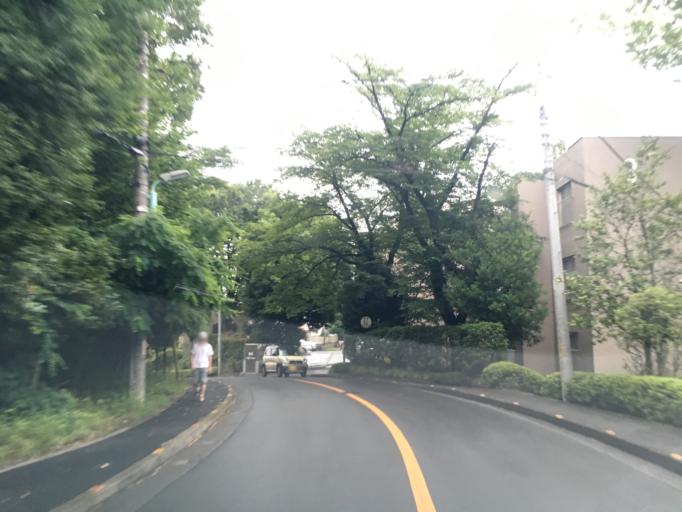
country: JP
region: Saitama
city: Tokorozawa
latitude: 35.7848
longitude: 139.4383
